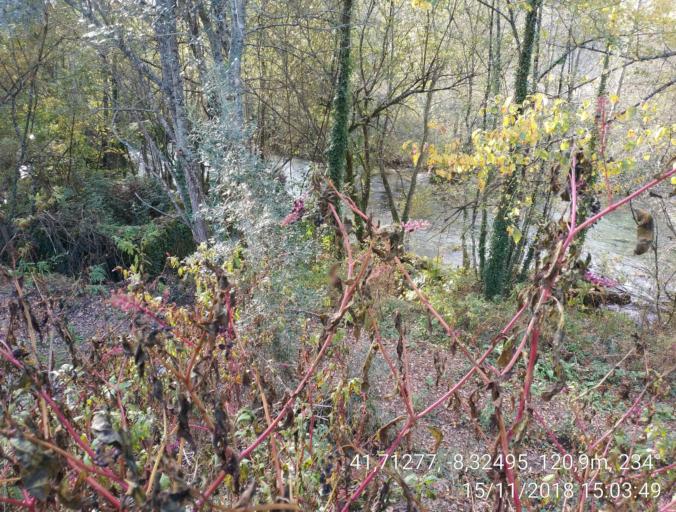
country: PT
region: Braga
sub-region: Terras de Bouro
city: Terras de Bouro
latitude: 41.7128
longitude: -8.3250
